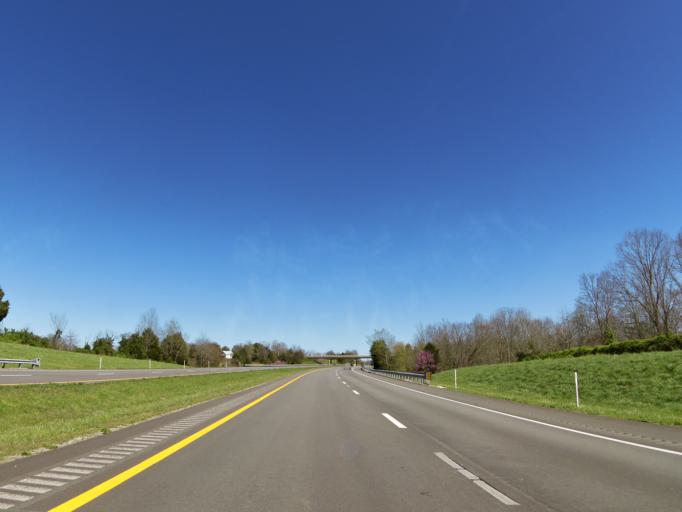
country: US
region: Kentucky
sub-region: Pulaski County
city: Somerset
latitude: 37.0976
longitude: -84.7274
